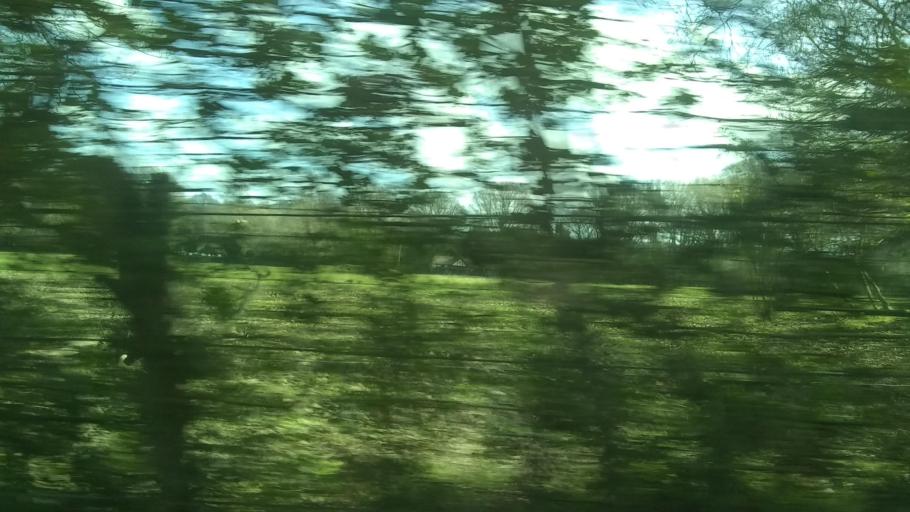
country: GB
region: England
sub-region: Worcestershire
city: Bewdley
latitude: 52.3734
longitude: -2.3923
